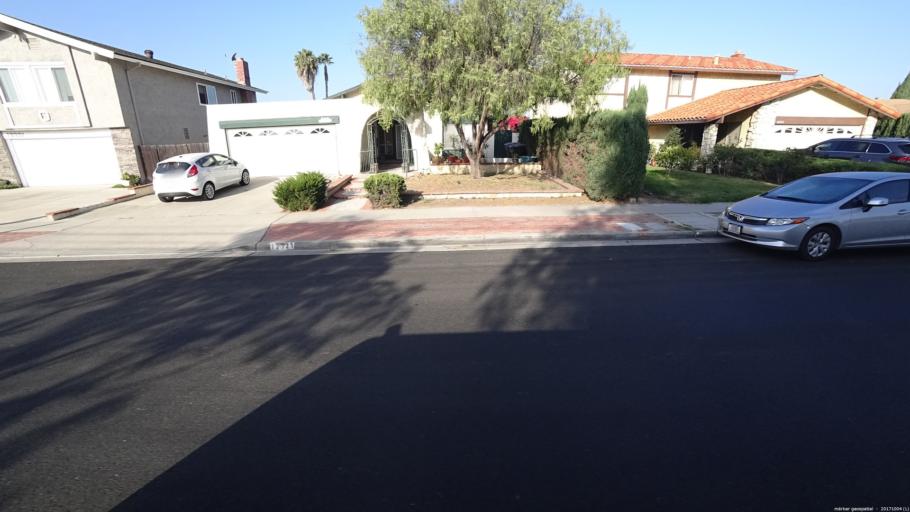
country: US
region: California
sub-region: Orange County
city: Garden Grove
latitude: 33.7841
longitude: -117.9192
